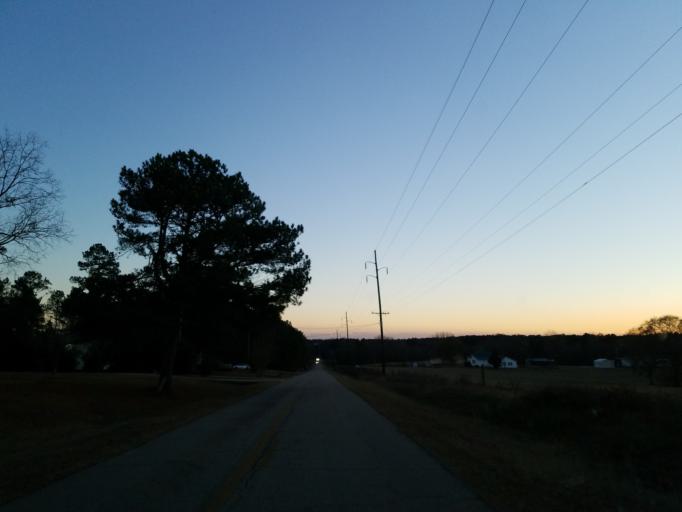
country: US
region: Georgia
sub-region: Monroe County
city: Forsyth
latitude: 33.0015
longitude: -83.8789
